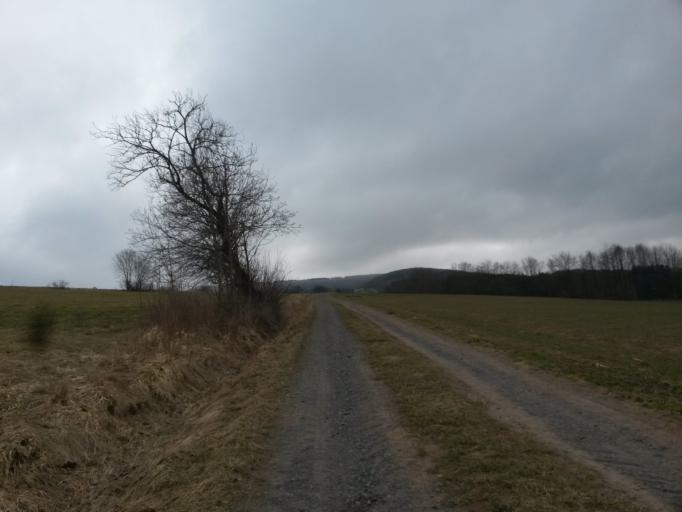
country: DE
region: Hesse
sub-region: Regierungsbezirk Kassel
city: Hilders
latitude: 50.5402
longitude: 9.9959
